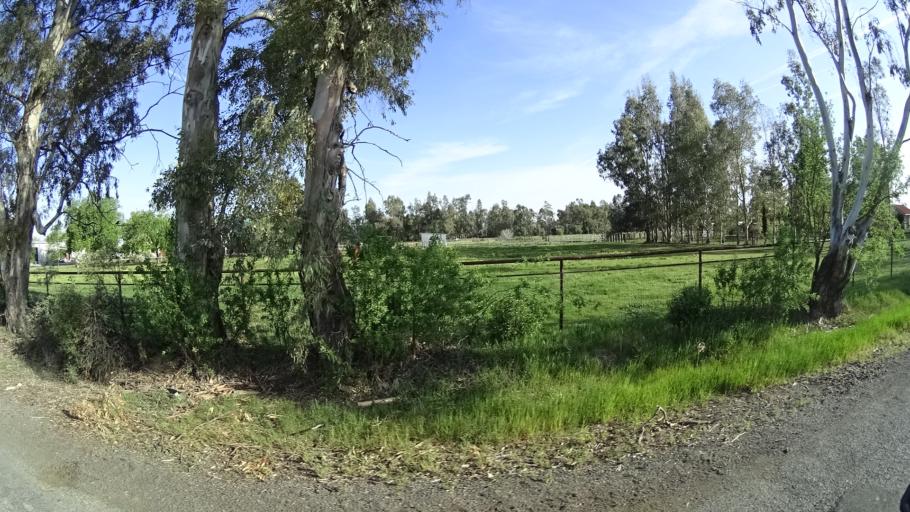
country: US
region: California
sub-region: Glenn County
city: Orland
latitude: 39.7151
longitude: -122.2145
